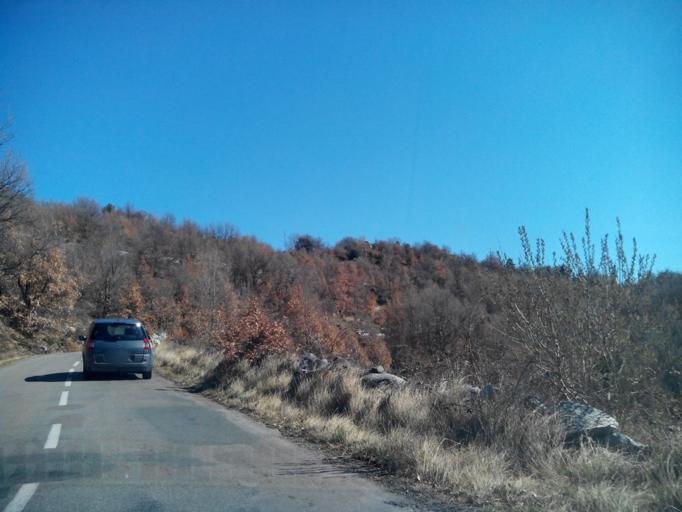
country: ES
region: Catalonia
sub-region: Provincia de Lleida
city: Lles de Cerdanya
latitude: 42.3791
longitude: 1.6877
